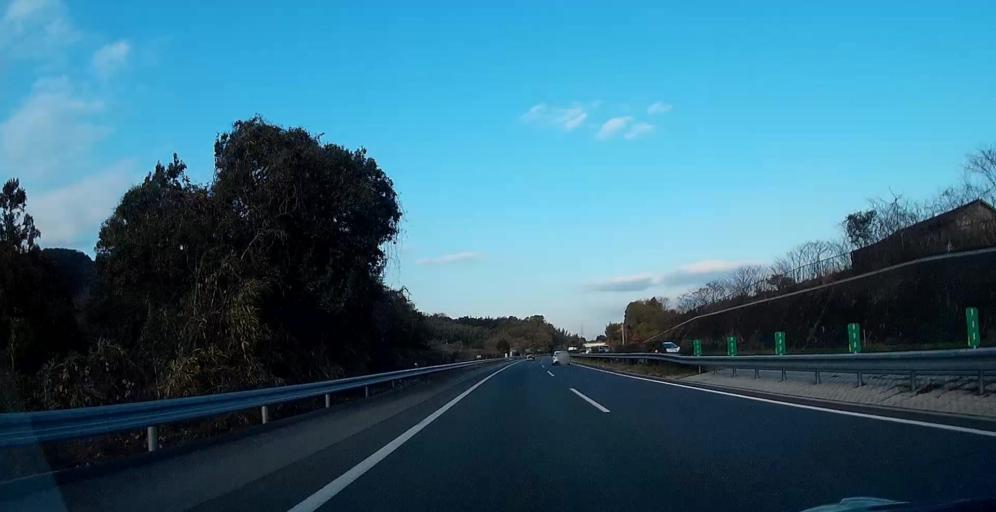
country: JP
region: Kumamoto
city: Uto
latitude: 32.6731
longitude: 130.7172
